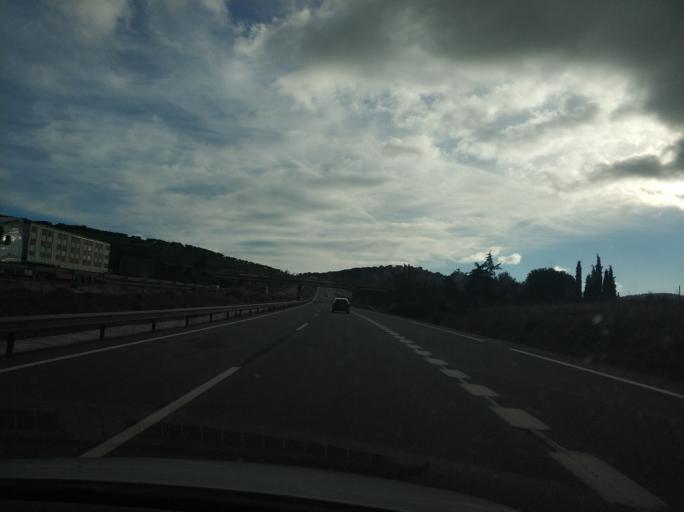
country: ES
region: Madrid
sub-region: Provincia de Madrid
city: Buitrago del Lozoya
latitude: 40.9662
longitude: -3.6416
